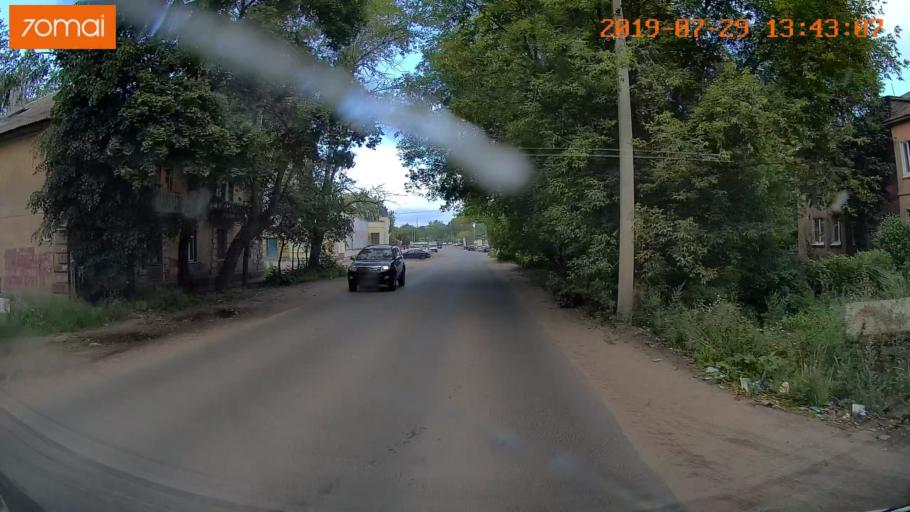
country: RU
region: Ivanovo
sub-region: Gorod Ivanovo
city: Ivanovo
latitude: 57.0028
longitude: 40.9308
